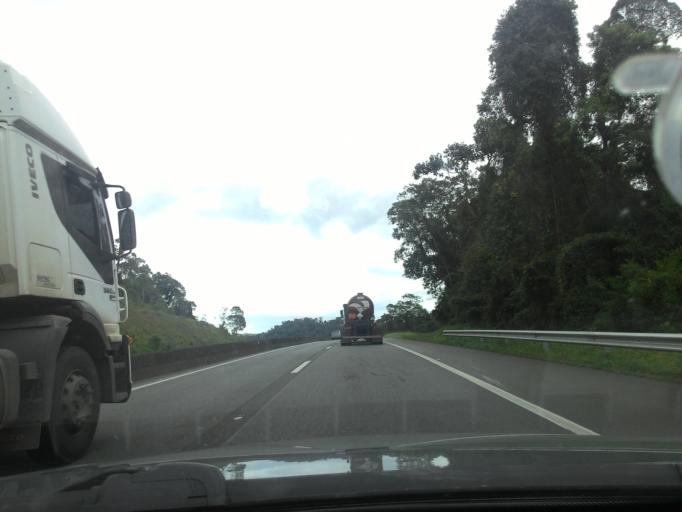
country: BR
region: Sao Paulo
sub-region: Cajati
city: Cajati
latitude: -24.9691
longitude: -48.3828
